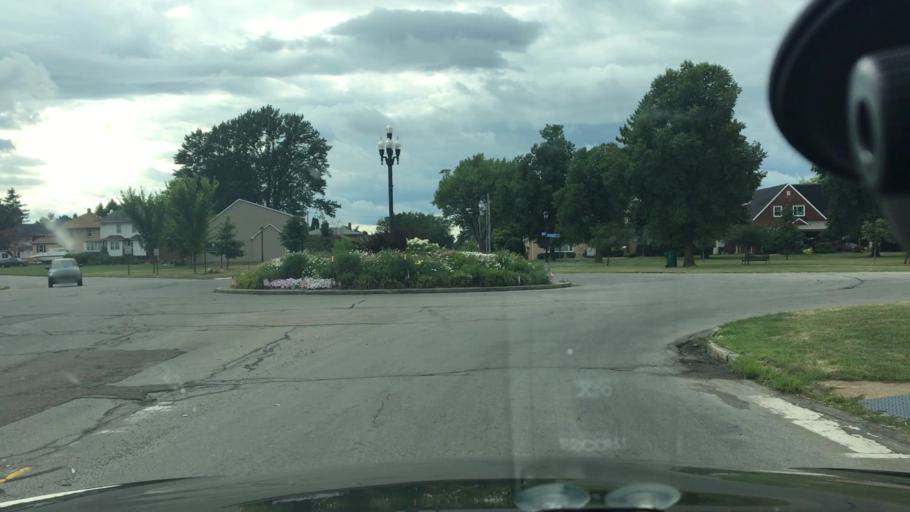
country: US
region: New York
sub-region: Erie County
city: Lackawanna
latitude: 42.8320
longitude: -78.8148
